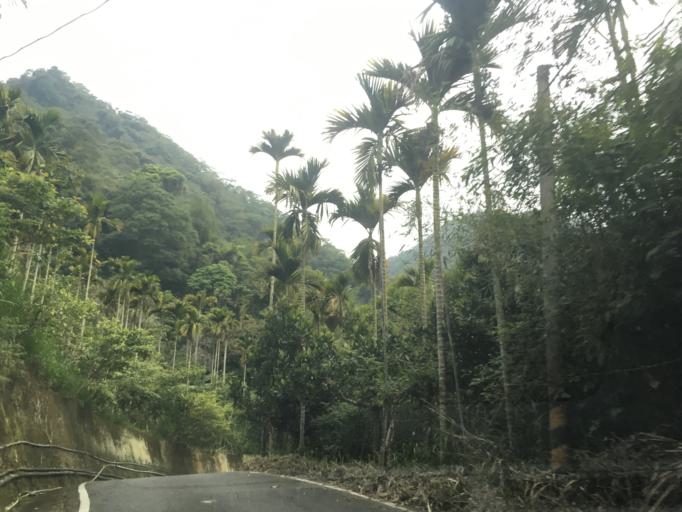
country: TW
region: Taiwan
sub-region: Nantou
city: Puli
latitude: 23.9470
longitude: 120.8522
